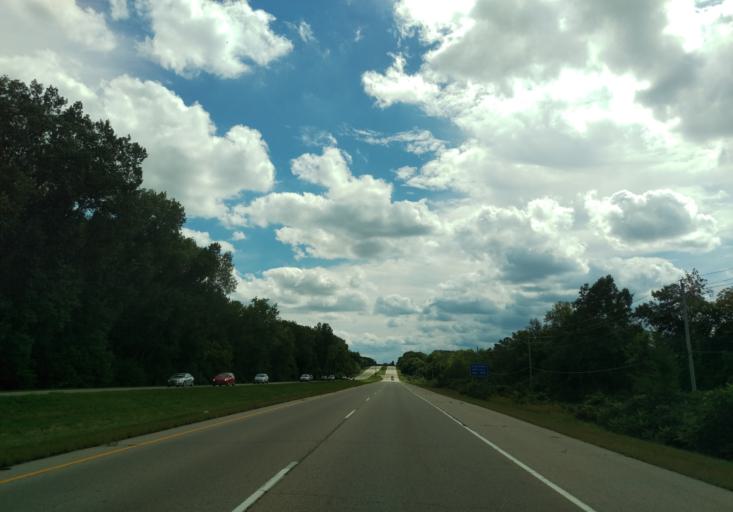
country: US
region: Wisconsin
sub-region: Dane County
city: Maple Bluff
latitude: 43.1485
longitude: -89.3996
